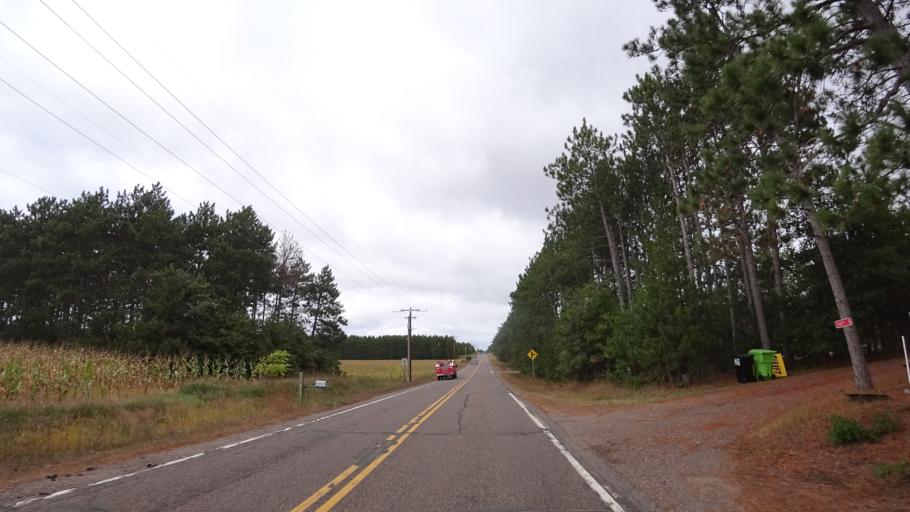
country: US
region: Wisconsin
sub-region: Chippewa County
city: Lake Wissota
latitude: 44.9562
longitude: -91.2678
